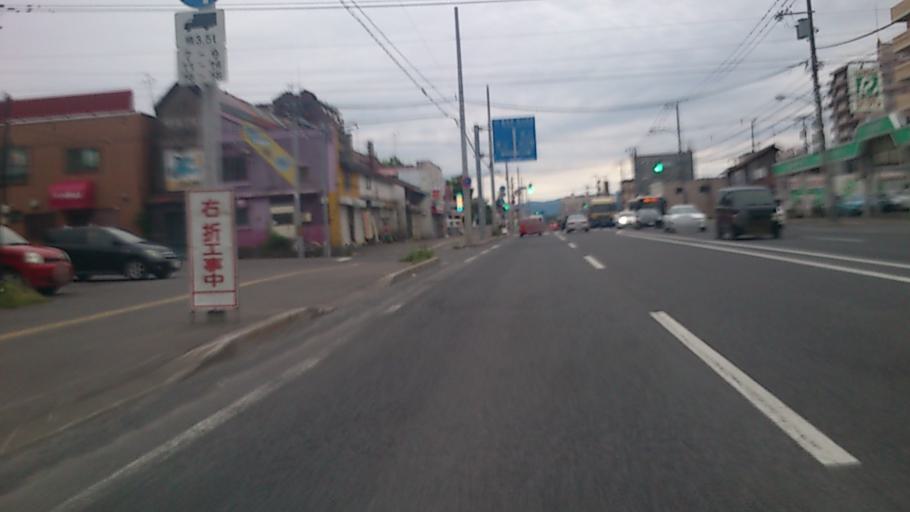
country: JP
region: Hokkaido
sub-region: Asahikawa-shi
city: Asahikawa
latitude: 43.7672
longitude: 142.3795
